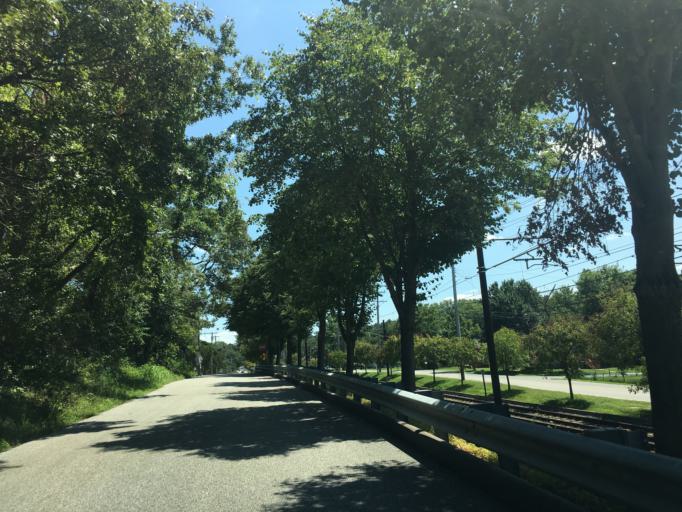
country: US
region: Maryland
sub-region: Anne Arundel County
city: Linthicum
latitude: 39.1948
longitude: -76.6513
